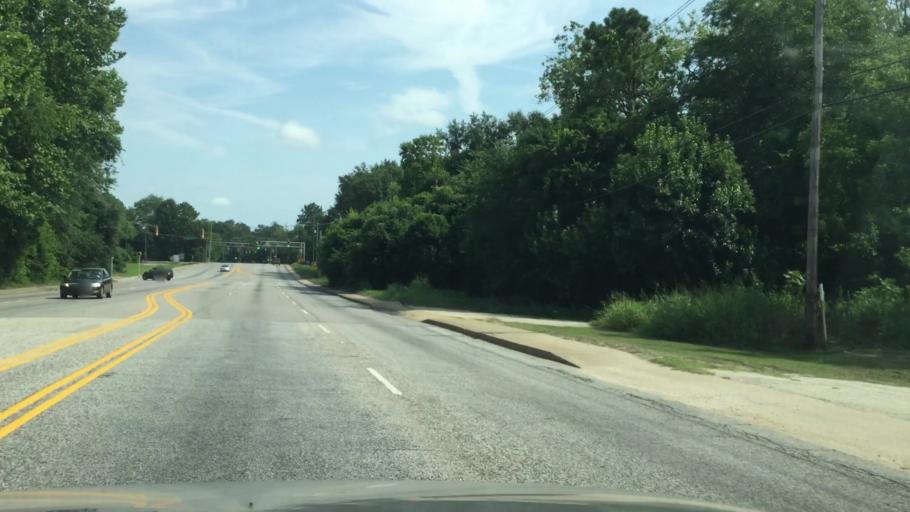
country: US
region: South Carolina
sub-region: Sumter County
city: South Sumter
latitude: 33.9088
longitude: -80.3540
